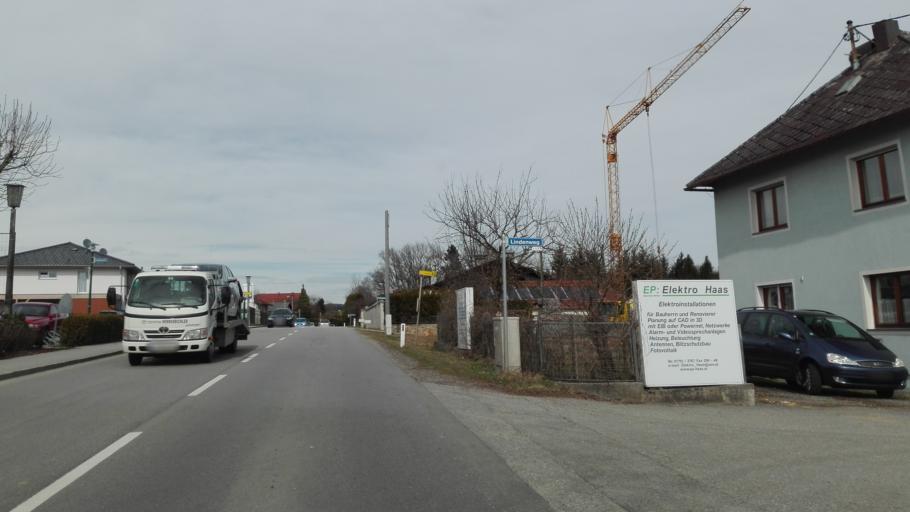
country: AT
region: Upper Austria
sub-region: Politischer Bezirk Scharding
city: Scharding
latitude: 48.4746
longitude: 13.4509
